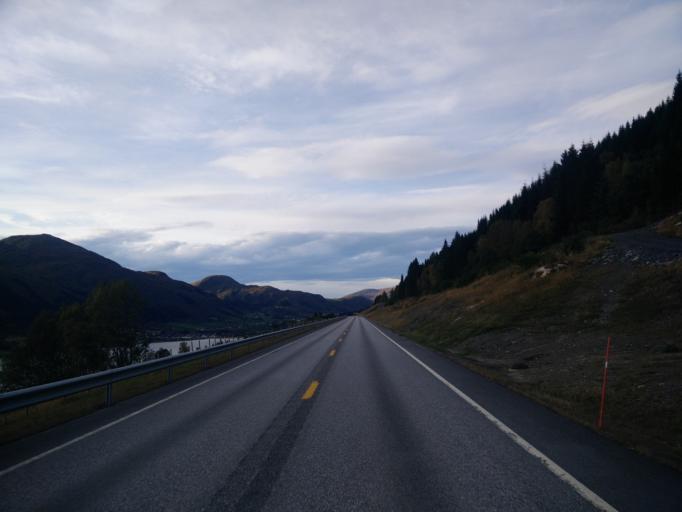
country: NO
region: More og Romsdal
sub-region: Gjemnes
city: Batnfjordsora
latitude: 62.9179
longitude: 7.6950
